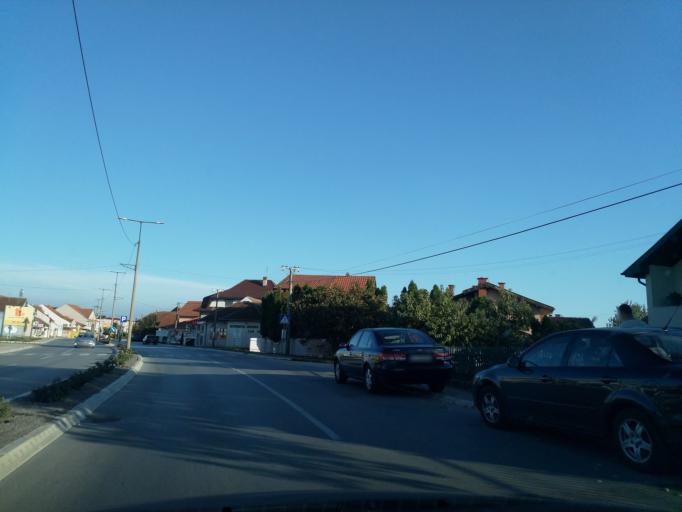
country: RS
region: Central Serbia
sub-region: Pomoravski Okrug
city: Svilajnac
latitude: 44.2328
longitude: 21.1875
